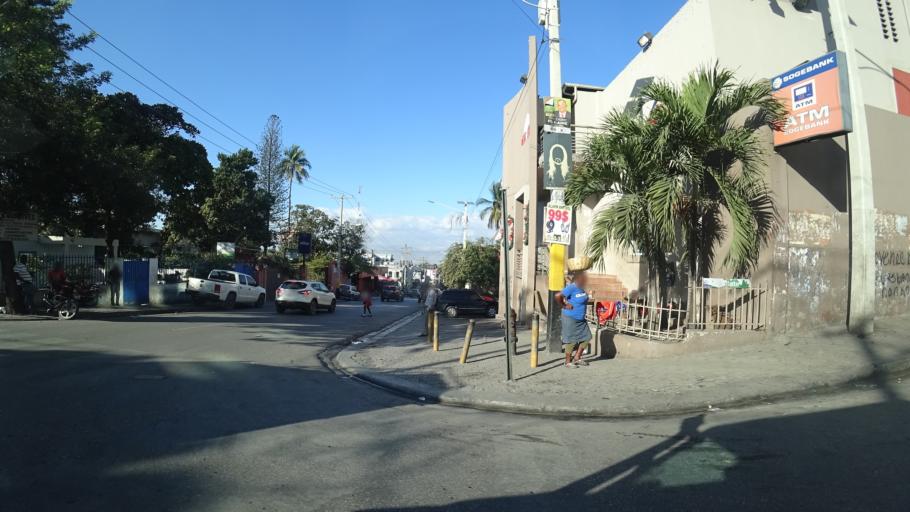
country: HT
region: Ouest
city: Petionville
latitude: 18.5143
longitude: -72.2884
